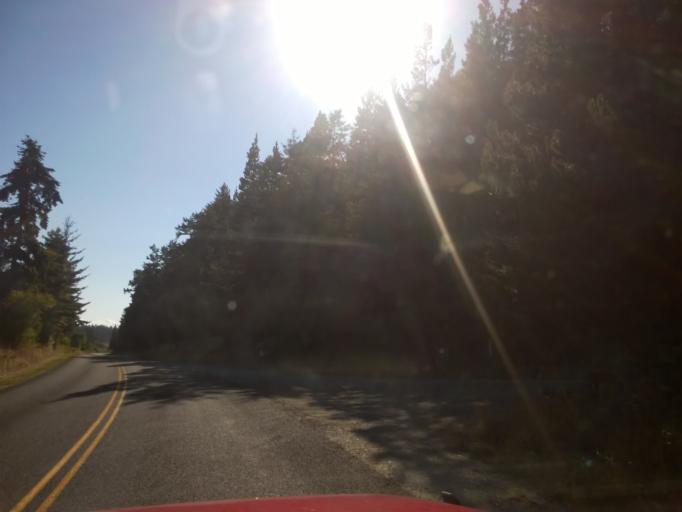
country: US
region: Washington
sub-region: Island County
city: Ault Field
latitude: 48.4441
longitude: -122.8264
